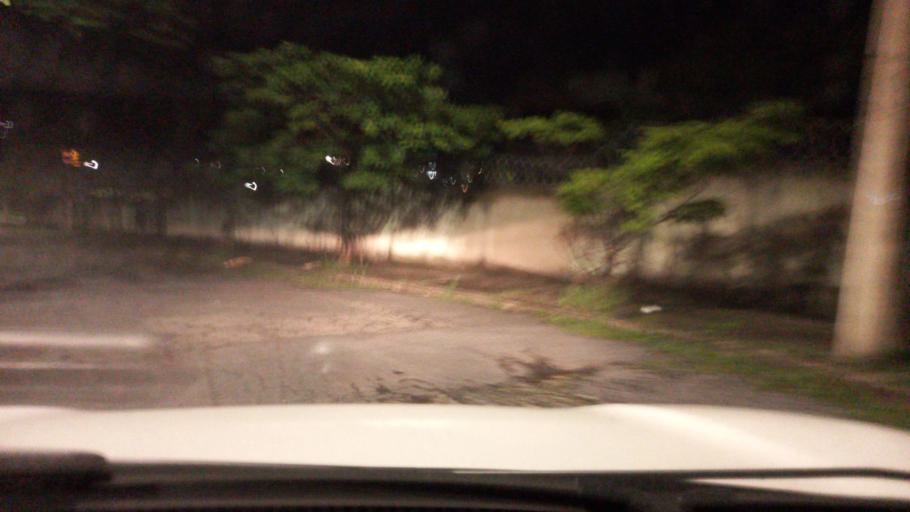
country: BR
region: Minas Gerais
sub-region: Belo Horizonte
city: Belo Horizonte
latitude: -19.9020
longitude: -43.9644
